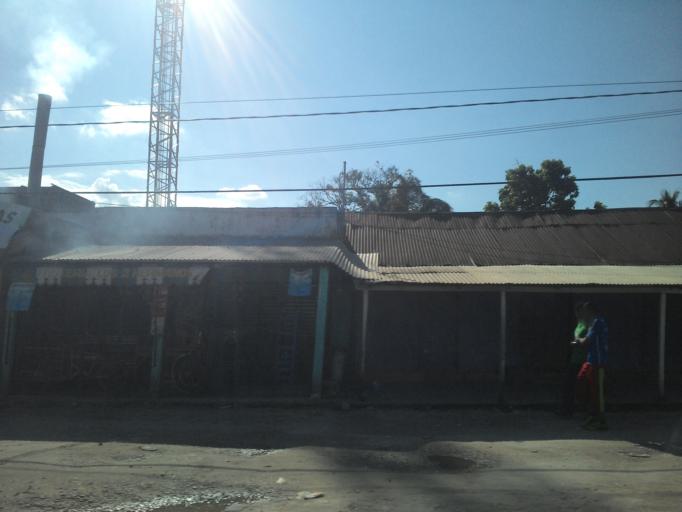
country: MX
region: Chiapas
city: Palenque
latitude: 17.5405
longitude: -91.9914
